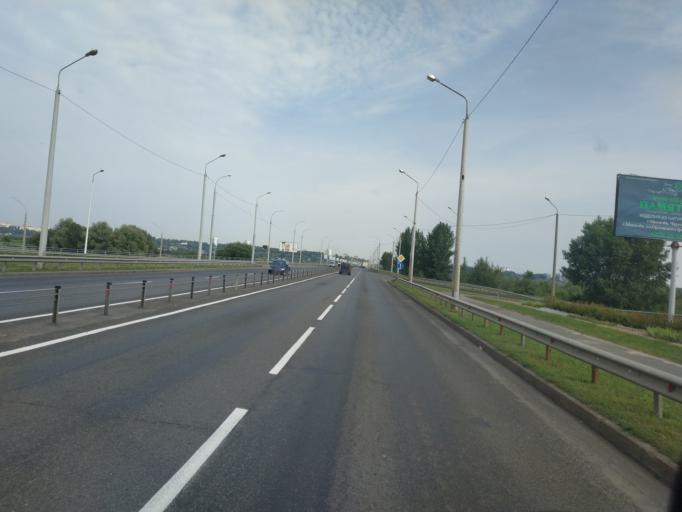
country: BY
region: Mogilev
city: Mahilyow
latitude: 53.8843
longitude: 30.3800
